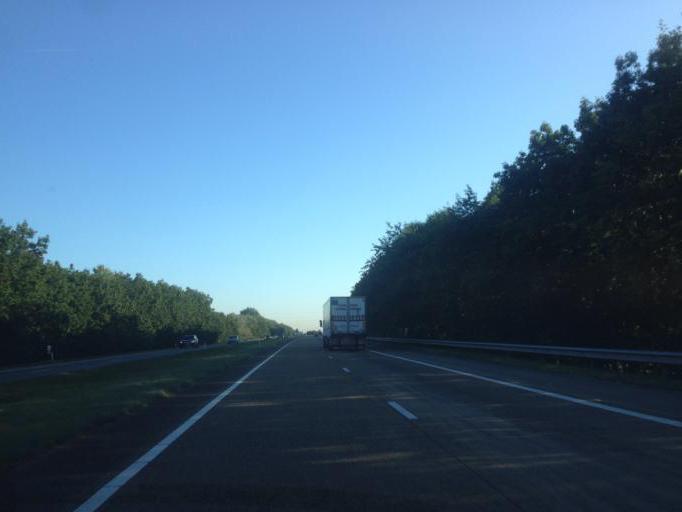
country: BE
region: Flanders
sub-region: Provincie Limburg
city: Overpelt
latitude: 51.2072
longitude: 5.3939
